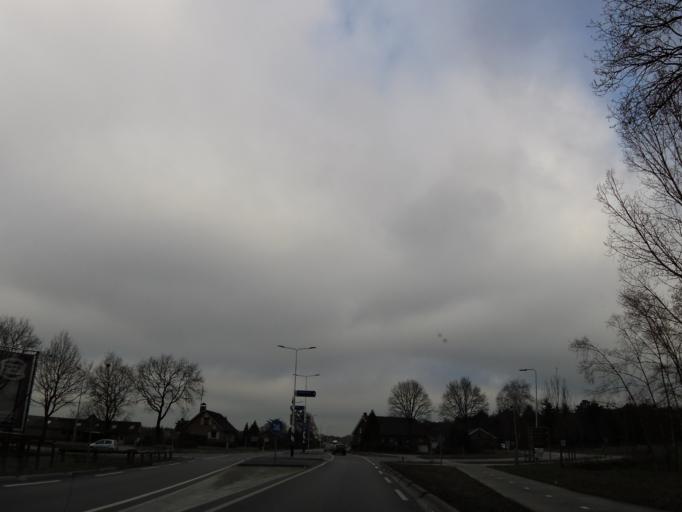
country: NL
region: Limburg
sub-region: Gemeente Peel en Maas
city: Maasbree
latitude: 51.3509
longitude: 5.9727
